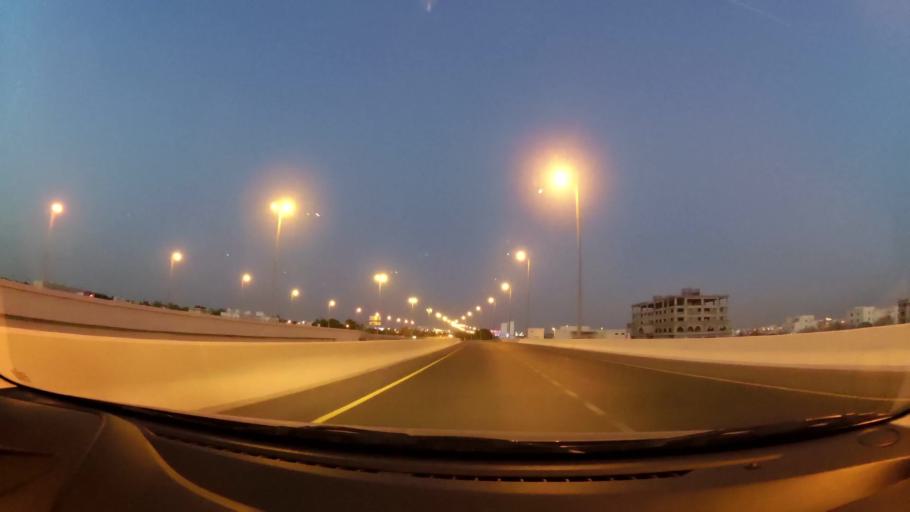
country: OM
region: Muhafazat Masqat
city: As Sib al Jadidah
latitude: 23.6578
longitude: 58.1909
